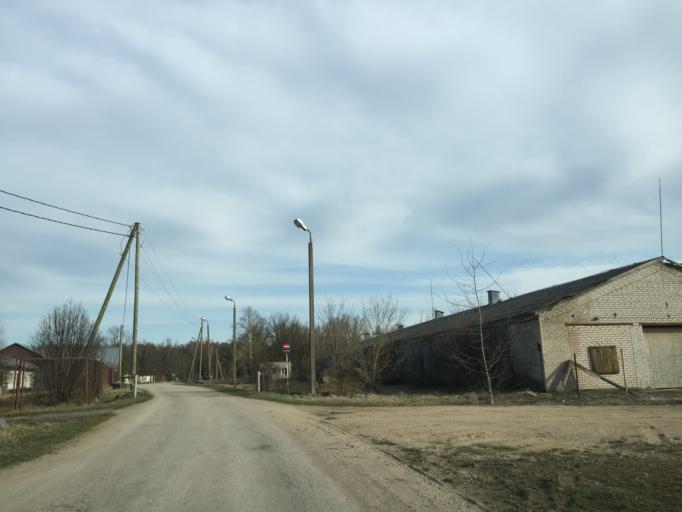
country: LV
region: Ogre
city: Ogre
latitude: 56.7832
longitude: 24.6587
